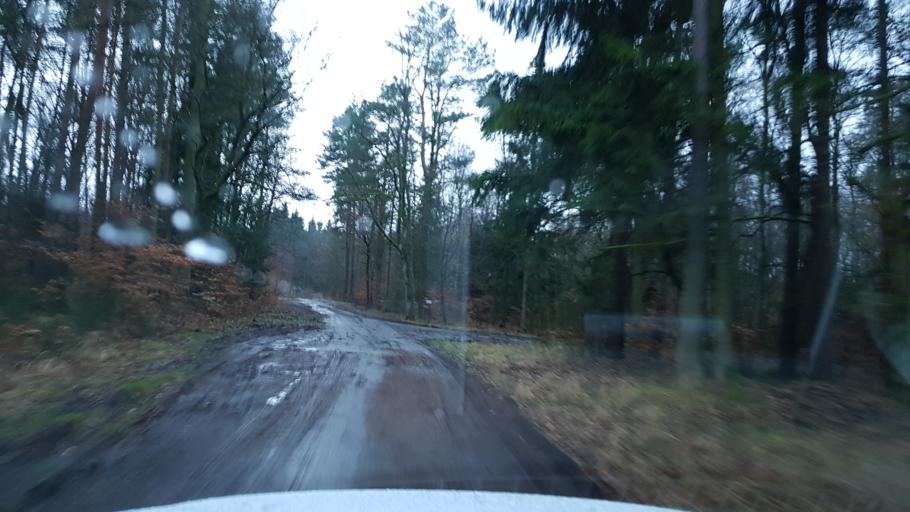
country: PL
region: West Pomeranian Voivodeship
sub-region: Powiat goleniowski
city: Osina
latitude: 53.5736
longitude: 15.0557
